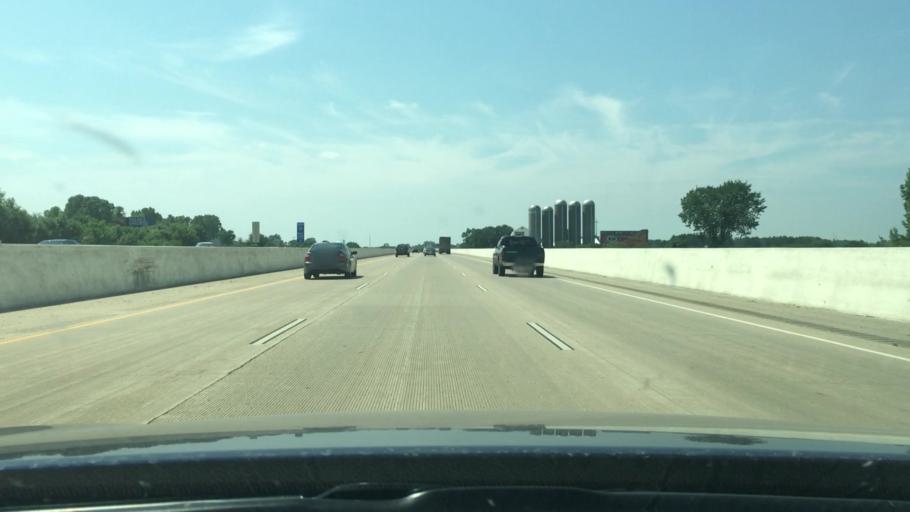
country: US
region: Wisconsin
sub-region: Winnebago County
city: Neenah
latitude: 44.1397
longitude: -88.4920
